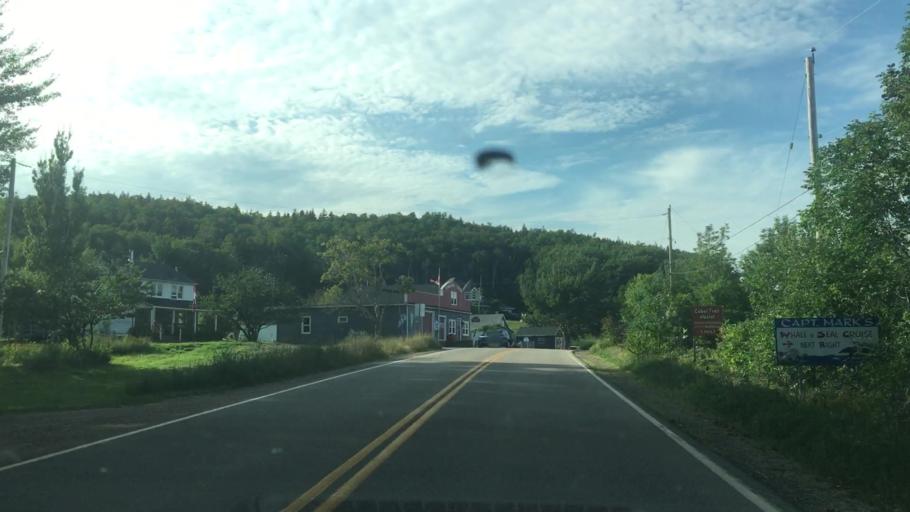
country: CA
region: Nova Scotia
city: Sydney Mines
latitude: 46.8221
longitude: -60.7987
